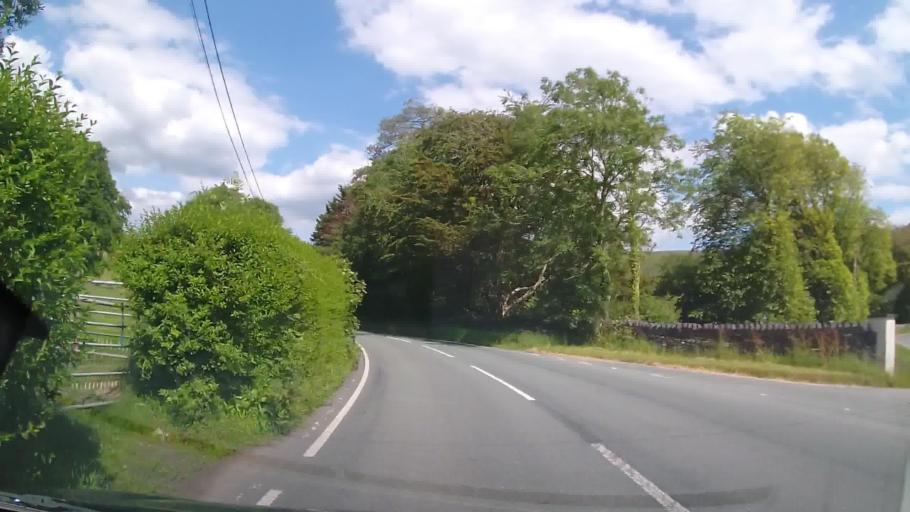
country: GB
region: Wales
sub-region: Gwynedd
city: Tywyn
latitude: 52.6121
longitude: -4.0368
